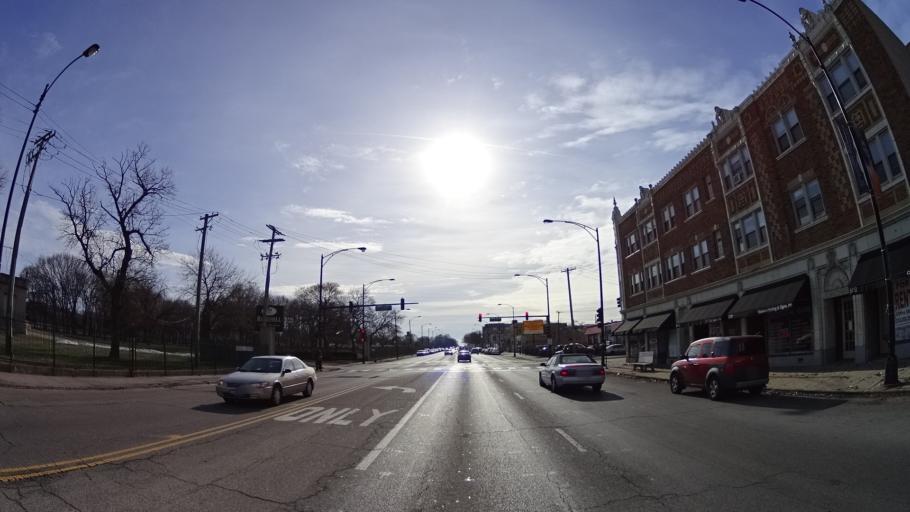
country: US
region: Illinois
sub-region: Cook County
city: Lincolnwood
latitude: 41.9836
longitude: -87.6895
